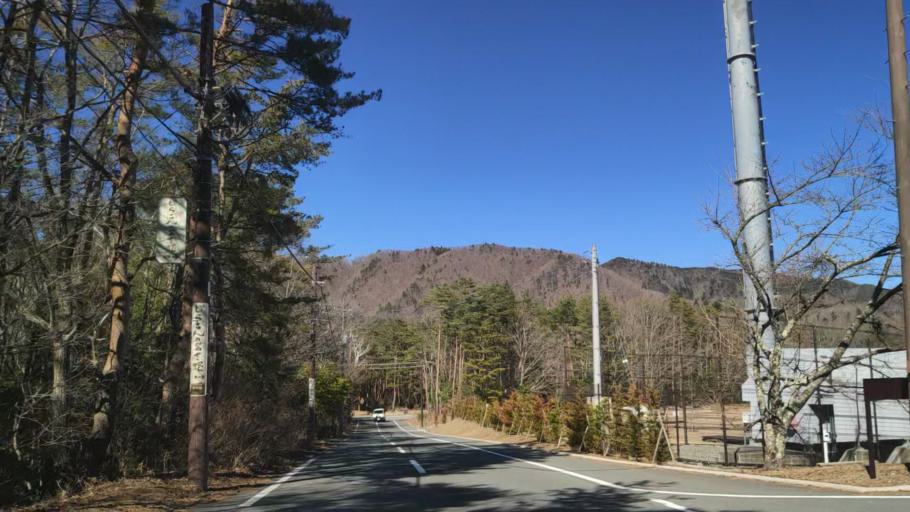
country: JP
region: Yamanashi
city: Fujikawaguchiko
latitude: 35.4766
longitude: 138.6857
